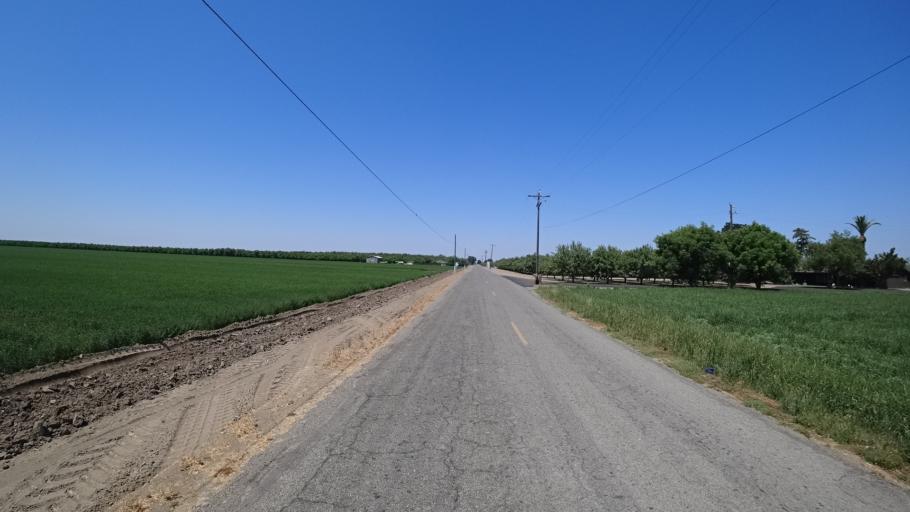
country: US
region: California
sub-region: Kings County
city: Armona
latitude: 36.3572
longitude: -119.7333
